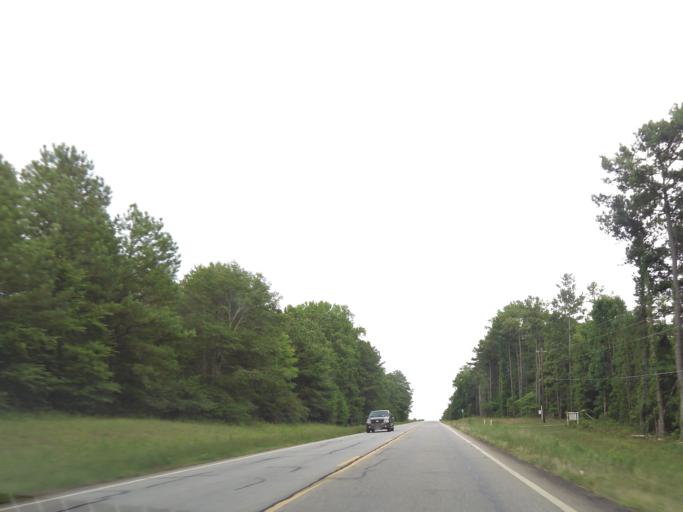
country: US
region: Georgia
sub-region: Bibb County
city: West Point
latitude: 32.8587
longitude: -83.7986
